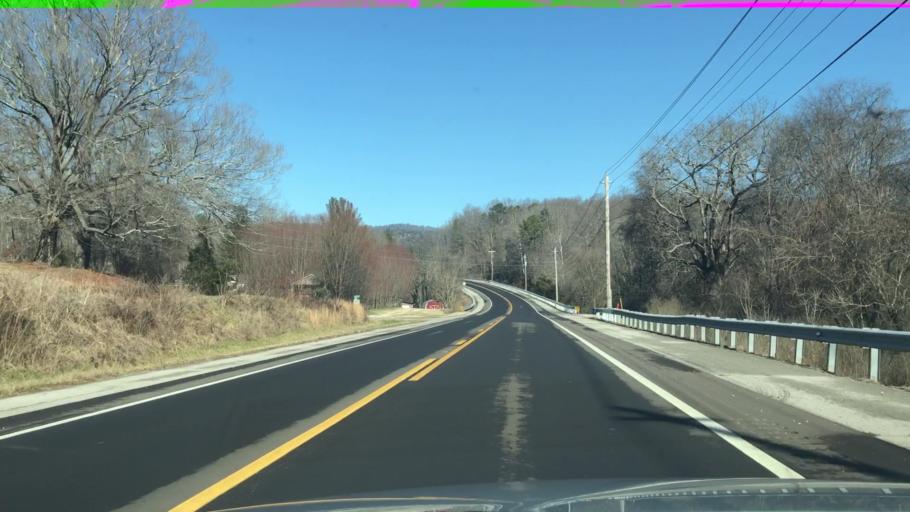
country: US
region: Tennessee
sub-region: Roane County
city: Midtown
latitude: 35.8870
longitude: -84.6174
